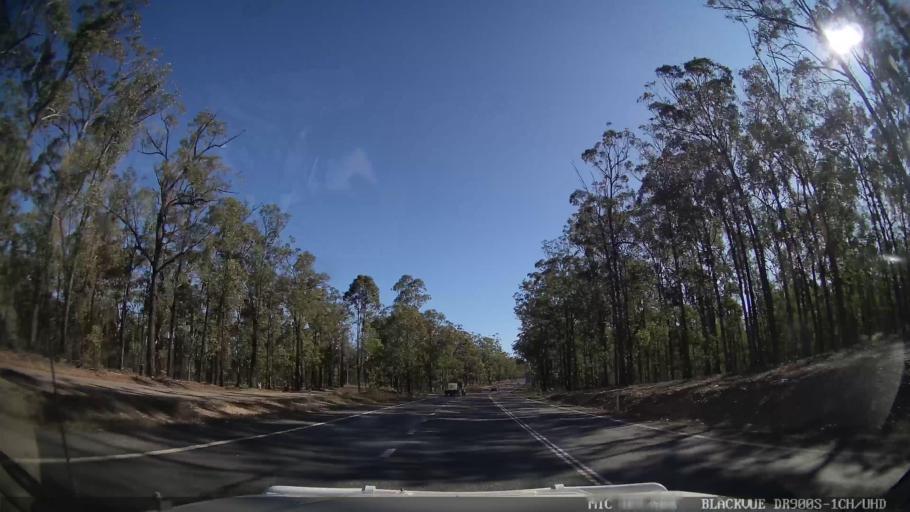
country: AU
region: Queensland
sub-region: Bundaberg
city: Childers
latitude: -25.2154
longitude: 152.0779
